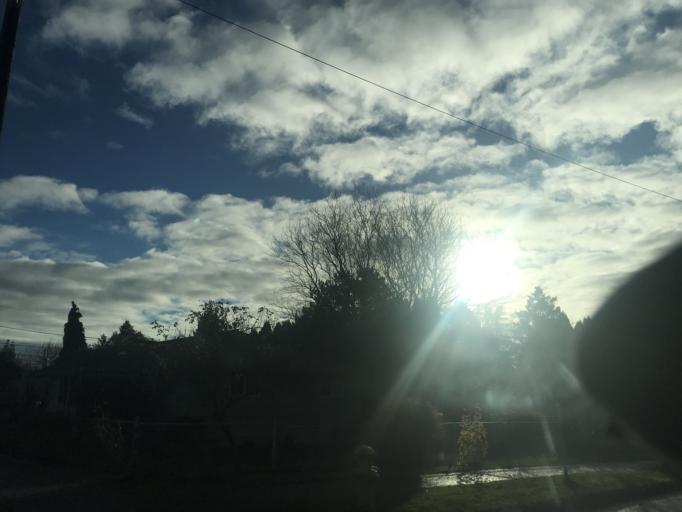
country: US
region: Washington
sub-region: King County
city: White Center
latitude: 47.5229
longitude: -122.3726
